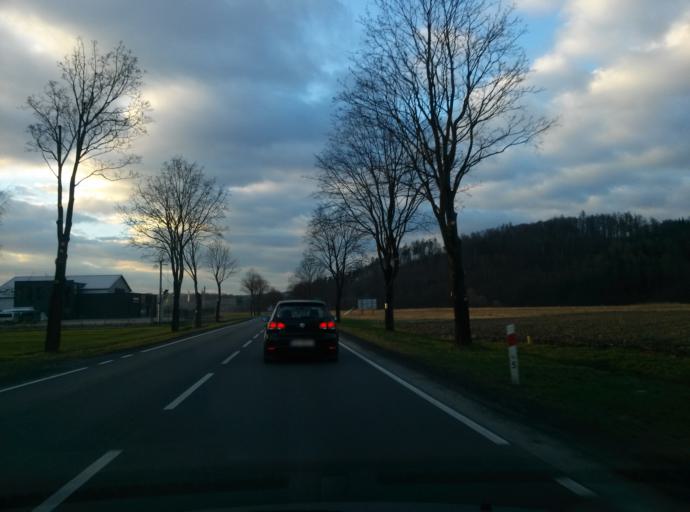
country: PL
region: Lesser Poland Voivodeship
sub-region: Powiat brzeski
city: Okocim
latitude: 49.9264
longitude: 20.5905
